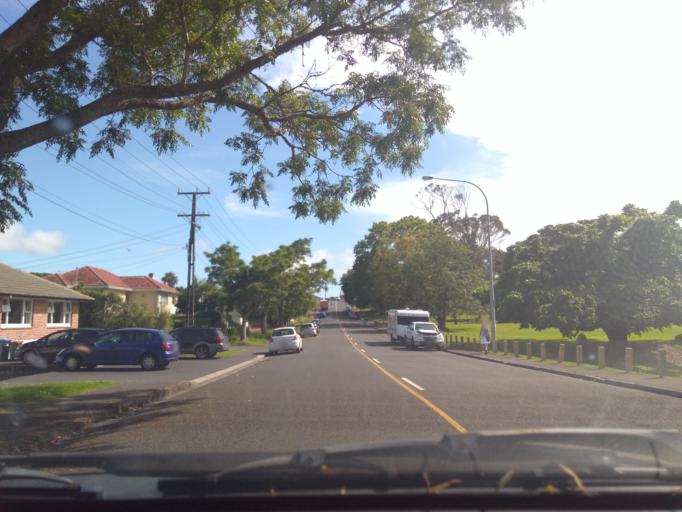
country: NZ
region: Auckland
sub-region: Auckland
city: Auckland
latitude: -36.8731
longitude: 174.7262
